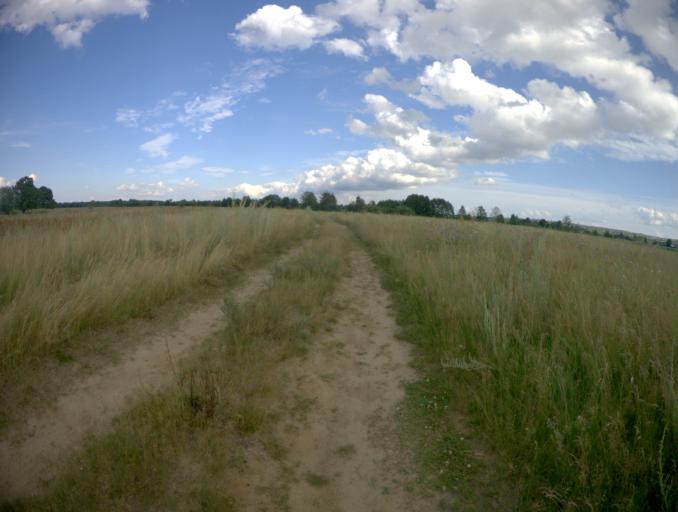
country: RU
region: Vladimir
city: Raduzhnyy
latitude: 56.0406
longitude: 40.3041
